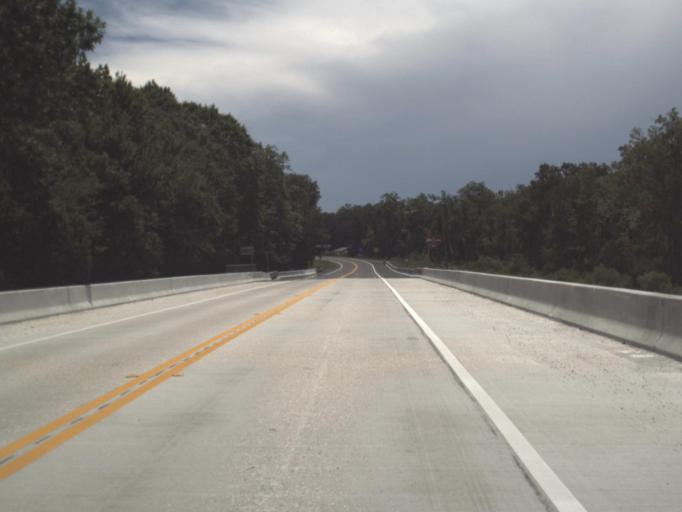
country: US
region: Florida
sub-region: Leon County
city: Woodville
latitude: 30.1454
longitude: -83.9714
